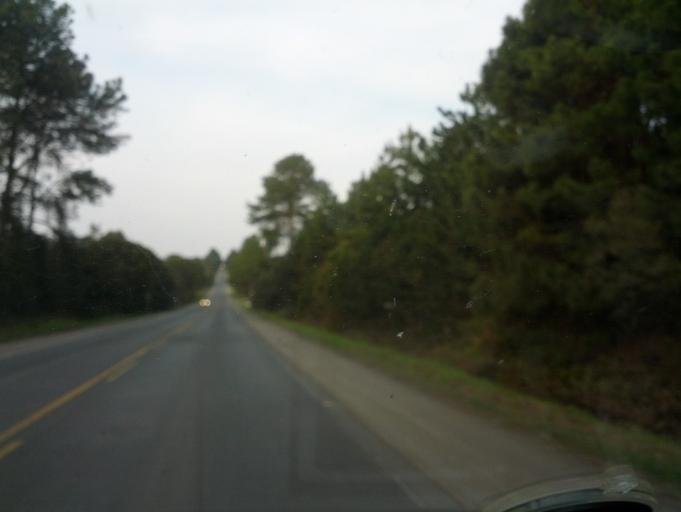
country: BR
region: Santa Catarina
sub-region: Otacilio Costa
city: Otacilio Costa
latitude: -27.3059
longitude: -50.1073
